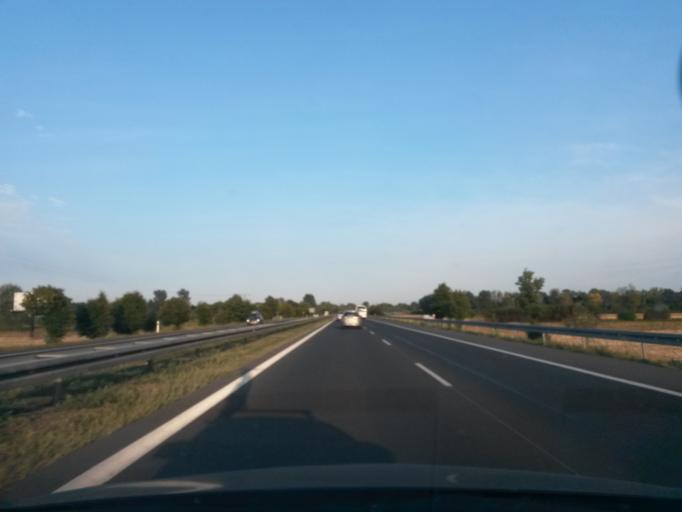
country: PL
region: Masovian Voivodeship
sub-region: Powiat nowodworski
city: Nowy Dwor Mazowiecki
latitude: 52.4162
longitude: 20.6817
